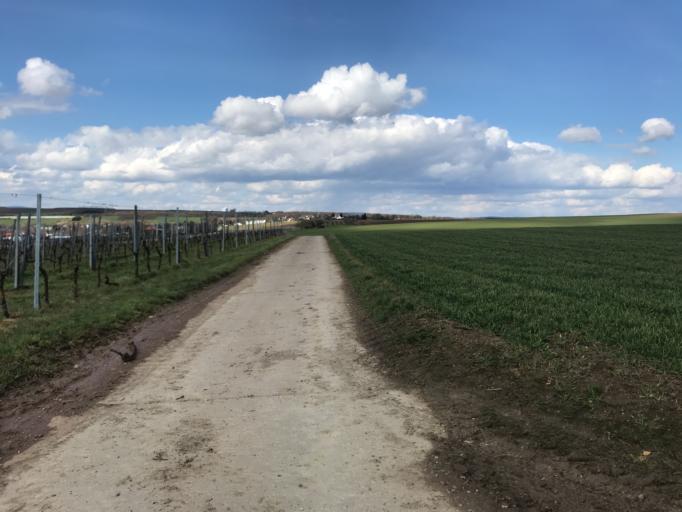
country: DE
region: Rheinland-Pfalz
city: Klein-Winternheim
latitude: 49.9333
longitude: 8.2279
